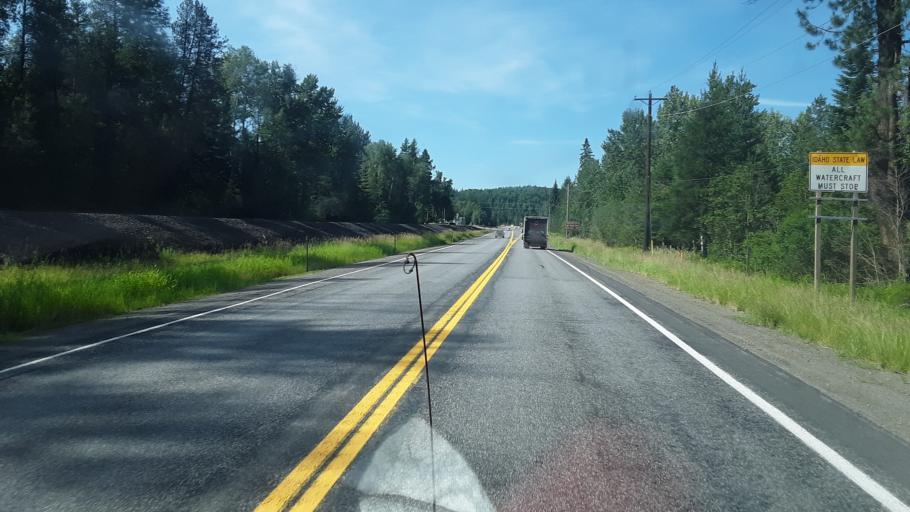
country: US
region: Idaho
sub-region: Bonner County
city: Ponderay
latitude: 48.4330
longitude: -116.4918
